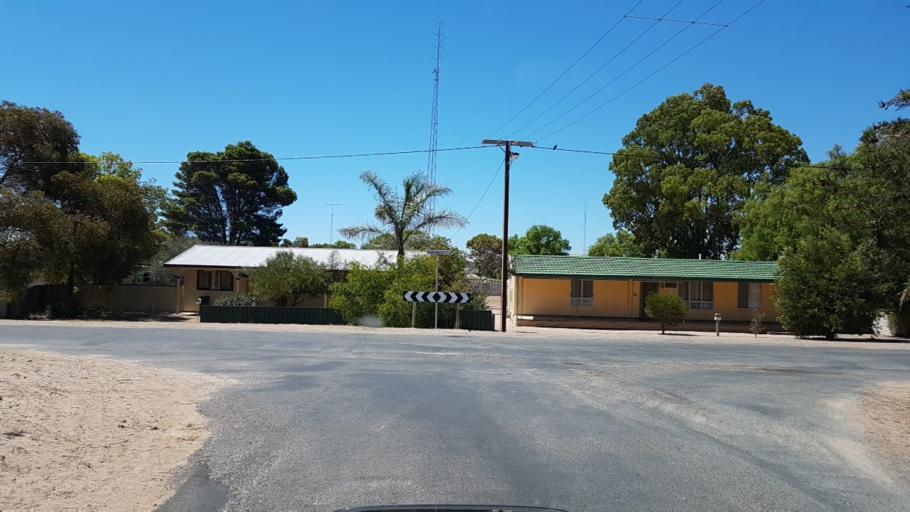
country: AU
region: South Australia
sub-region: Copper Coast
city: Wallaroo
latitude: -34.0528
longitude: 137.5652
